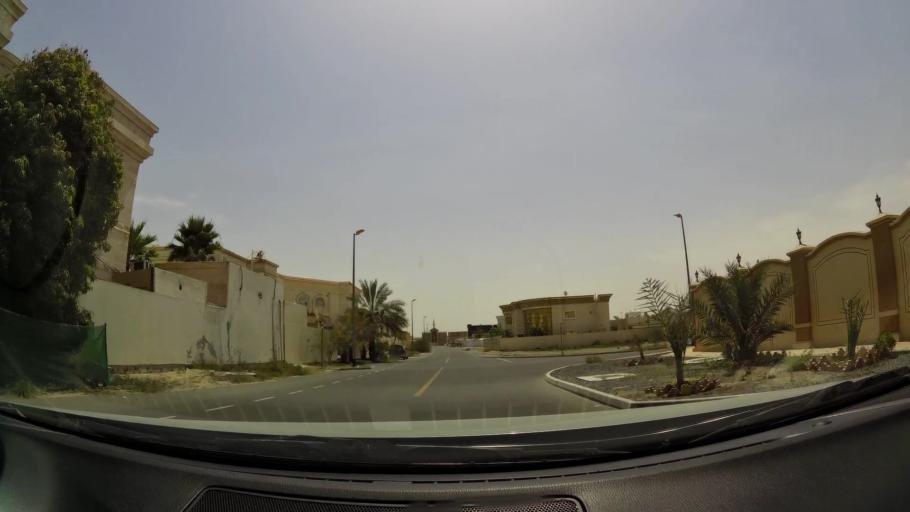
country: AE
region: Ash Shariqah
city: Sharjah
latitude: 25.1831
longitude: 55.4175
